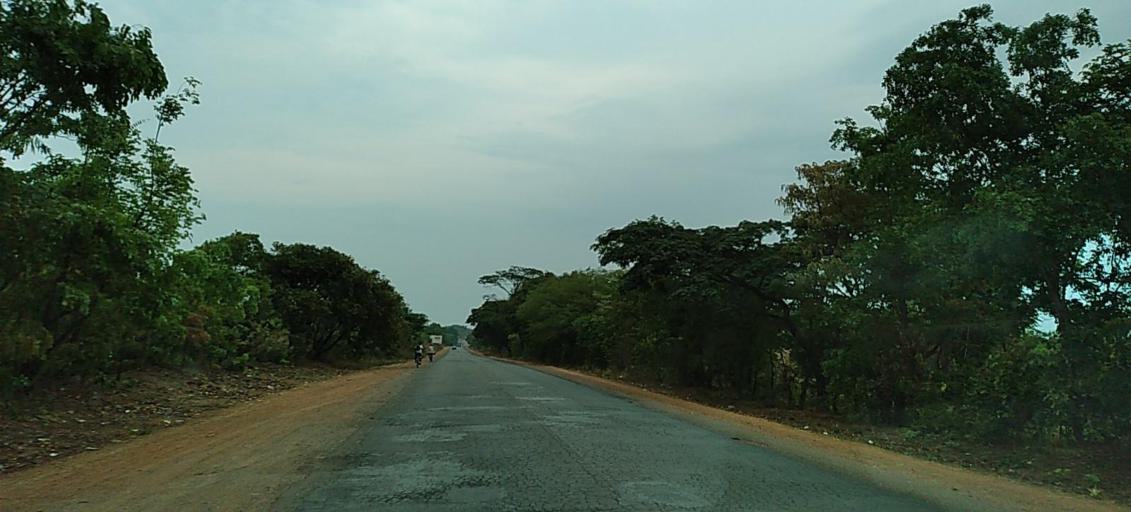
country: ZM
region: Copperbelt
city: Luanshya
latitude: -13.1075
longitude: 28.4272
